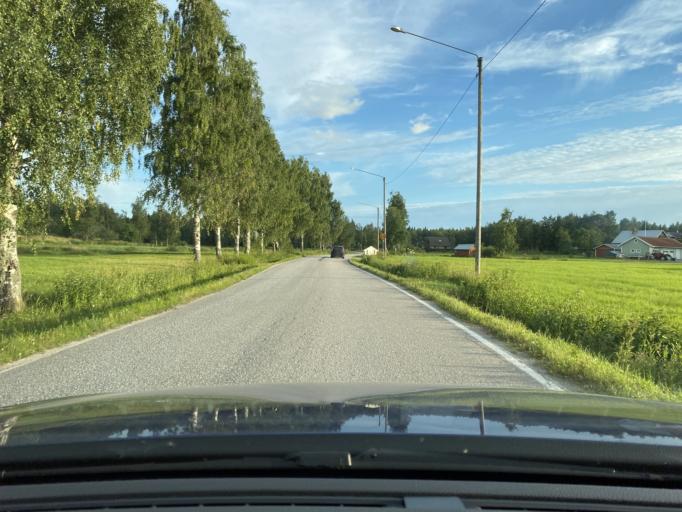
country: FI
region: Ostrobothnia
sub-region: Vaasa
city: Korsnaes
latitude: 62.9639
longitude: 21.1900
